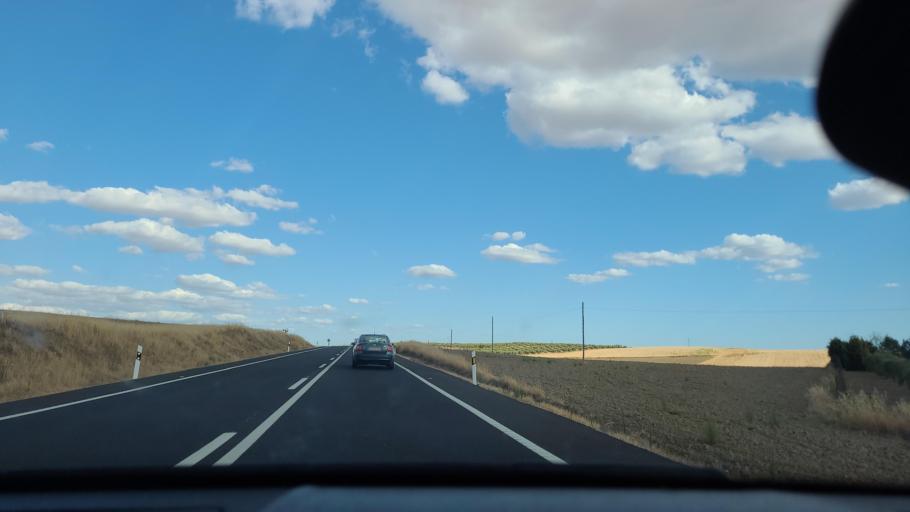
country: ES
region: Extremadura
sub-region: Provincia de Badajoz
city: Berlanga
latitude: 38.2697
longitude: -5.7922
